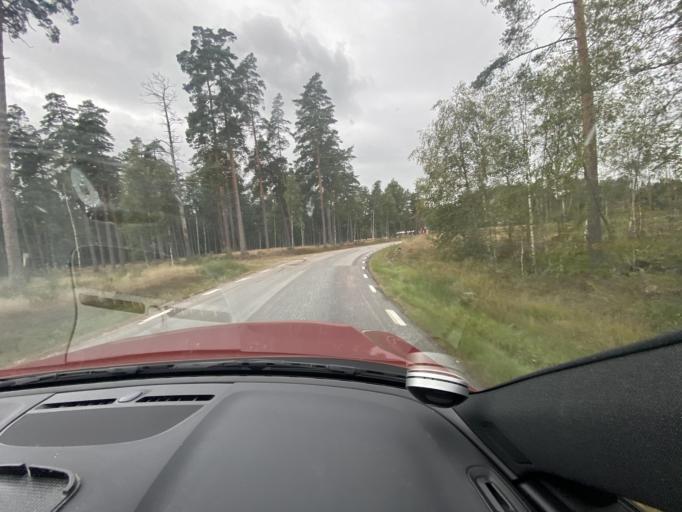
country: SE
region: Kronoberg
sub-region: Markaryds Kommun
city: Markaryd
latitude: 56.4915
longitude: 13.5804
